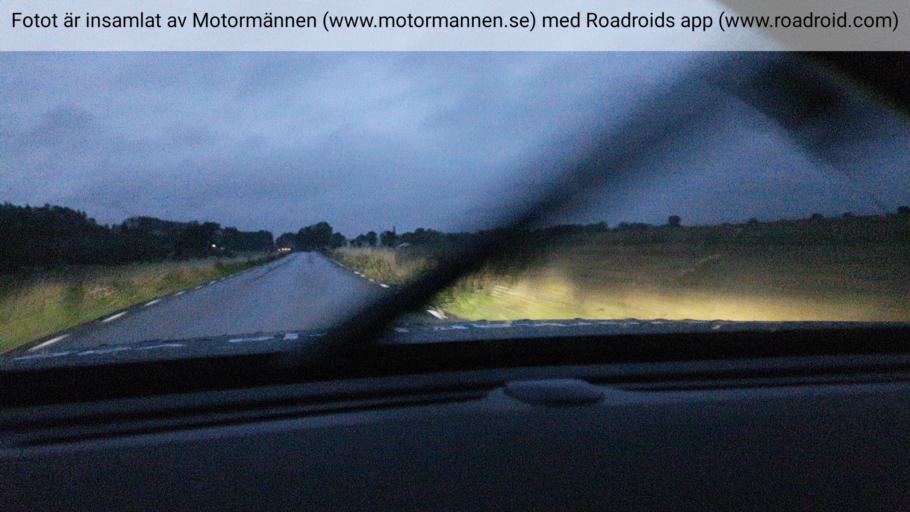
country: SE
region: Vaestra Goetaland
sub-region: Tidaholms Kommun
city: Tidaholm
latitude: 58.2107
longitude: 13.8264
